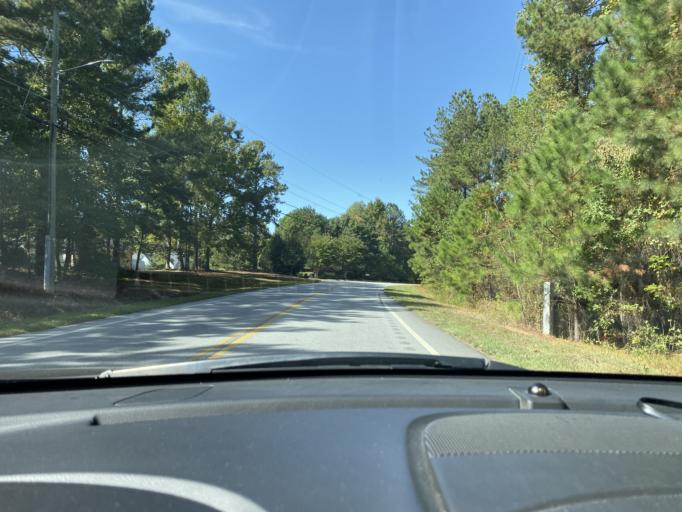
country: US
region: Georgia
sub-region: Gwinnett County
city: Grayson
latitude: 33.8987
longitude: -83.9128
